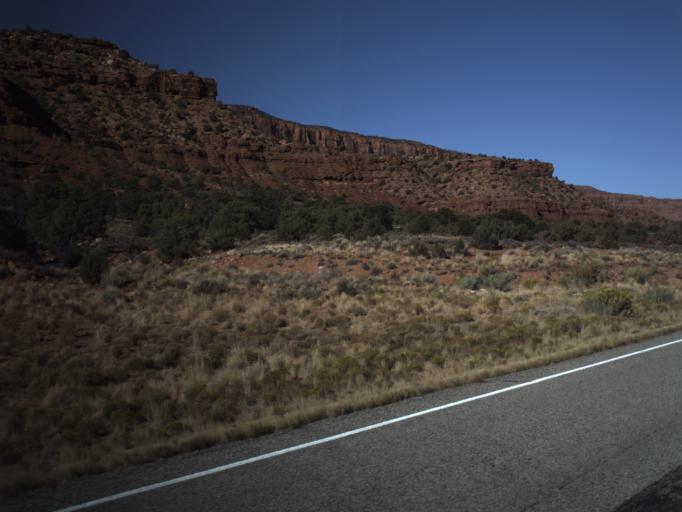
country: US
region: Utah
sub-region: San Juan County
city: Blanding
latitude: 37.6705
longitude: -110.2011
